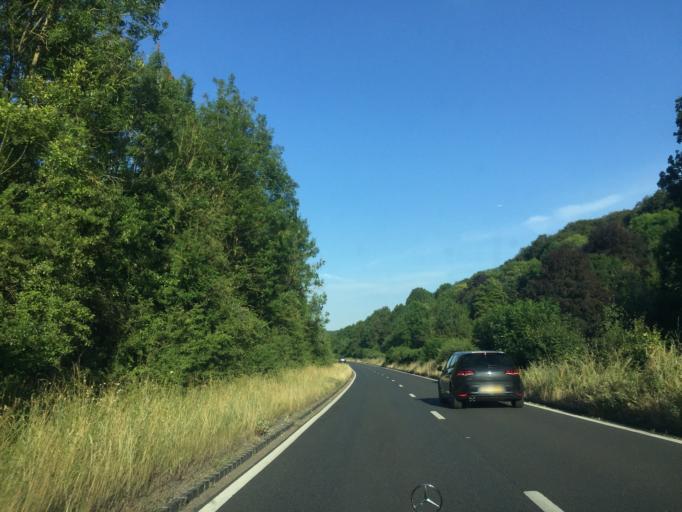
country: GB
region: England
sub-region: Oxfordshire
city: Rotherfield Peppard
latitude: 51.5566
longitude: -0.9412
